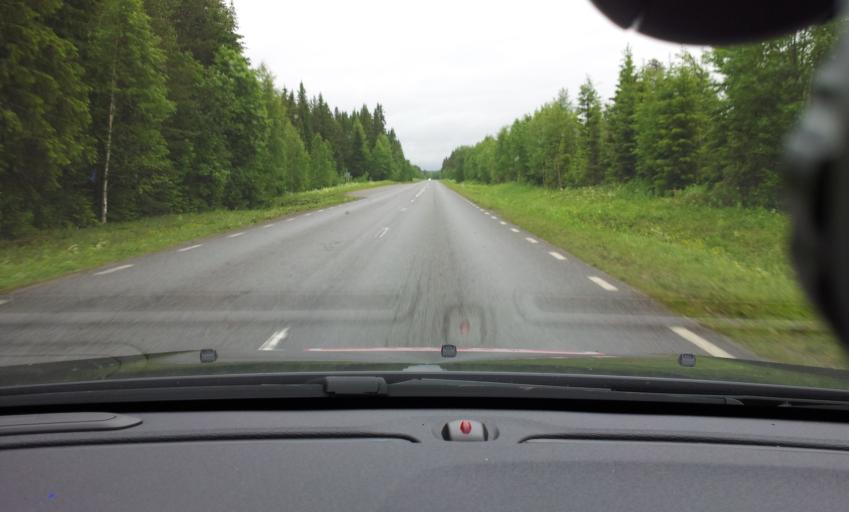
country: SE
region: Jaemtland
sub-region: Stroemsunds Kommun
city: Stroemsund
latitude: 63.6181
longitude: 15.2652
